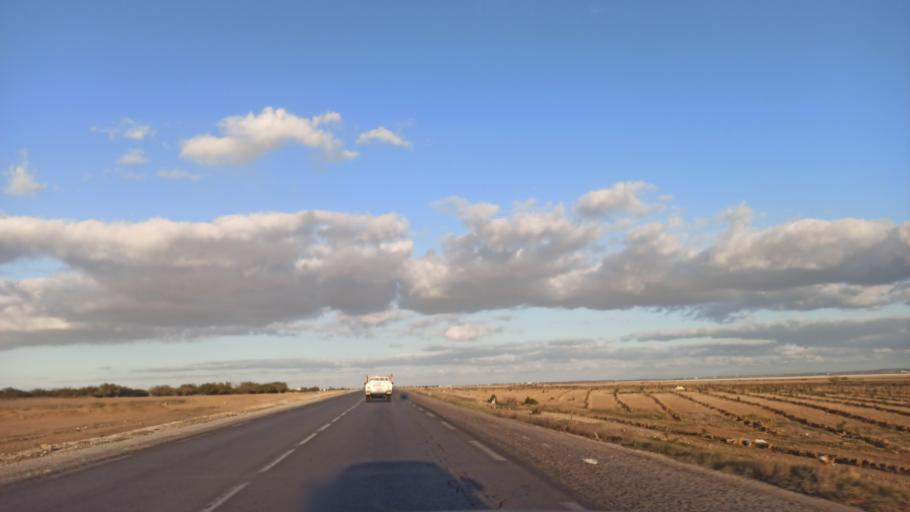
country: TN
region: Susah
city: Sidi Bou Ali
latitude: 35.8992
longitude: 10.2586
